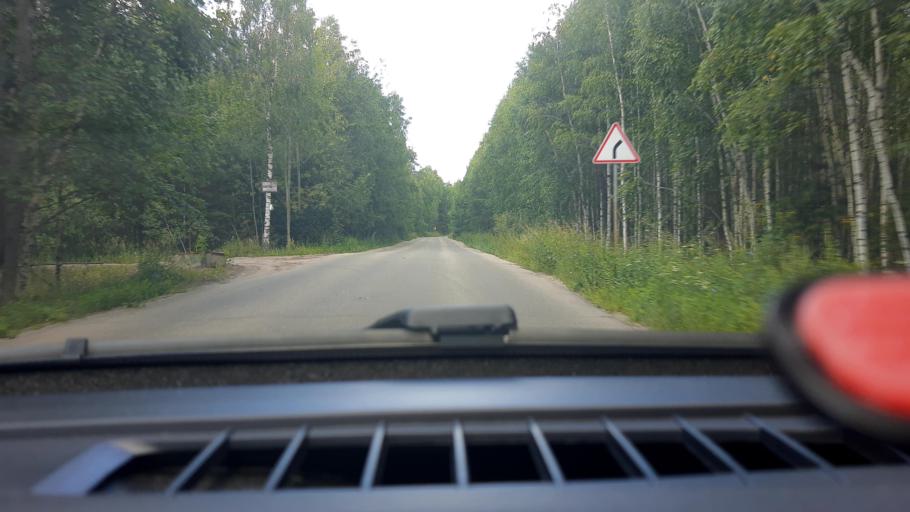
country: RU
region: Nizjnij Novgorod
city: Babino
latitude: 56.3145
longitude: 43.6260
